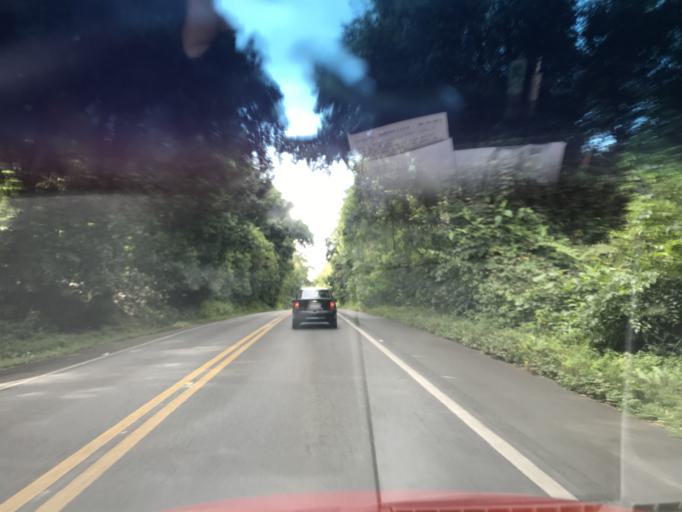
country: BR
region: Bahia
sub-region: Urucuca
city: Urucuca
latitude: -14.6302
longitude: -39.3337
